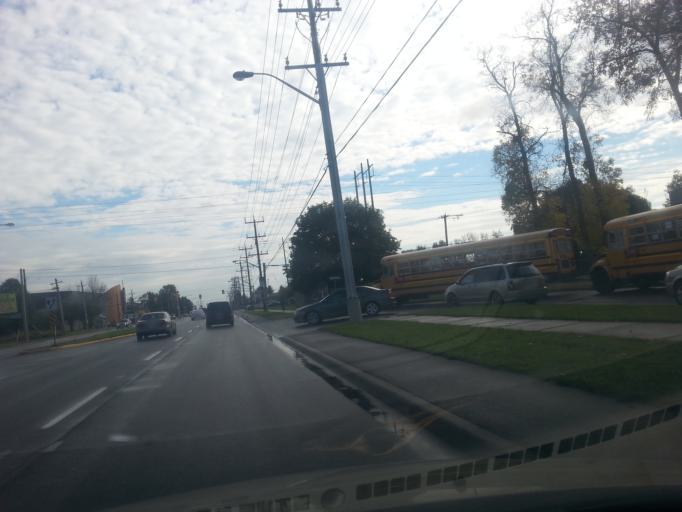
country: CA
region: Ontario
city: Bells Corners
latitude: 45.3281
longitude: -75.7806
